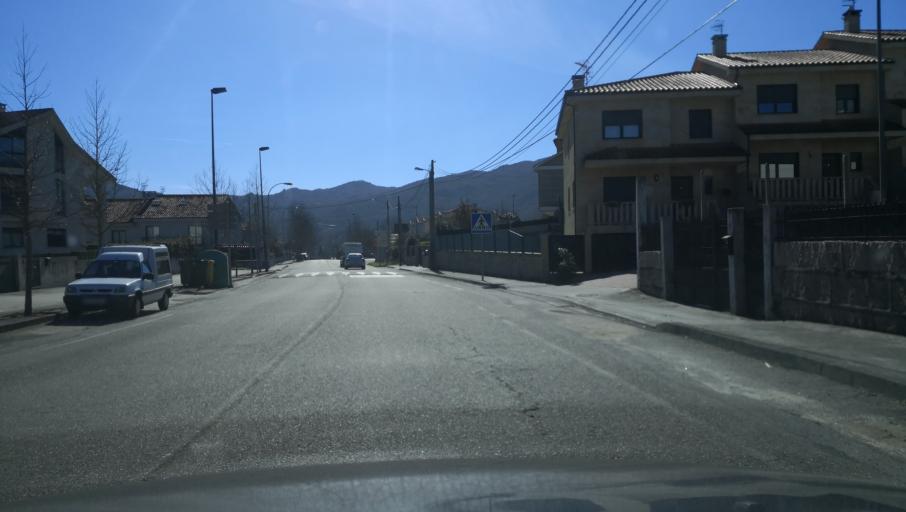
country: ES
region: Galicia
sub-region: Provincia de Ourense
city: Allariz
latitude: 42.1952
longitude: -7.8075
